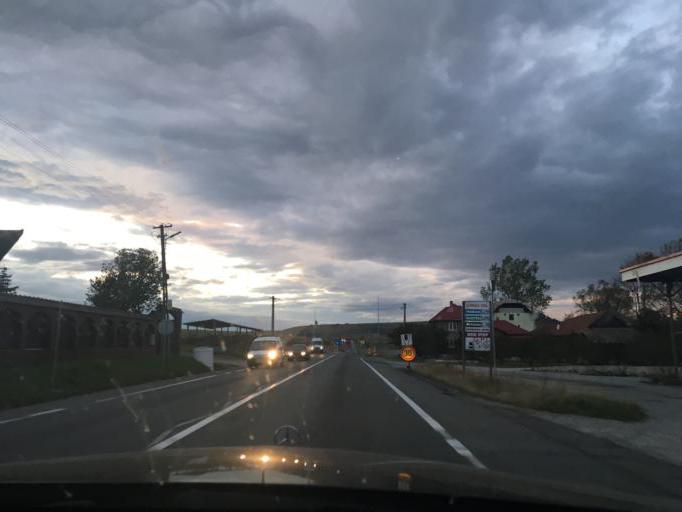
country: RO
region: Cluj
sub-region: Comuna Izvoru Crisului
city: Izvoru Crisului
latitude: 46.8163
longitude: 23.1777
